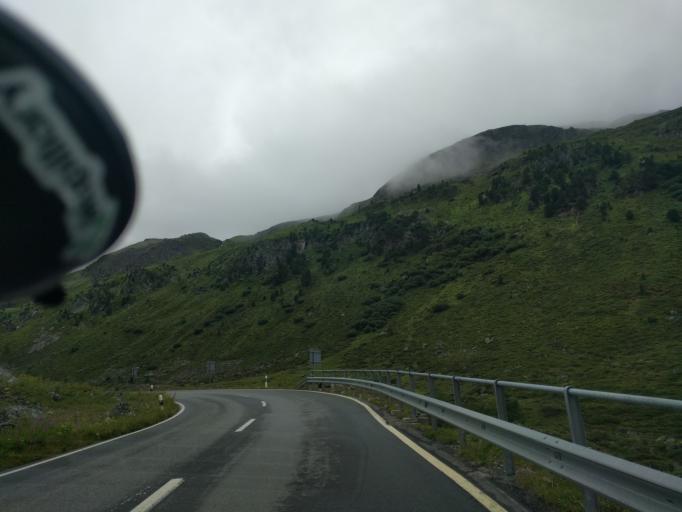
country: CH
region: Grisons
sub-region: Praettigau/Davos District
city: Davos
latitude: 46.7858
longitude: 9.9202
